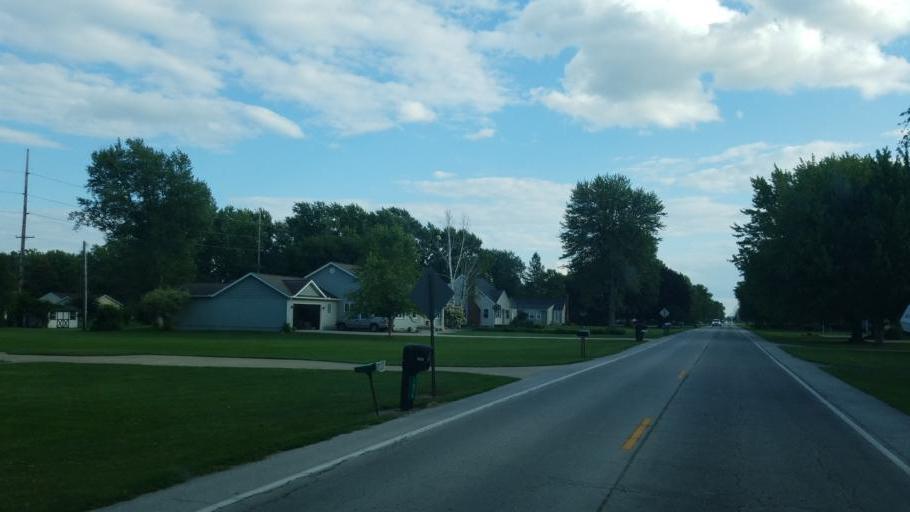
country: US
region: Ohio
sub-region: Sandusky County
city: Ballville
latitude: 41.3200
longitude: -83.1298
